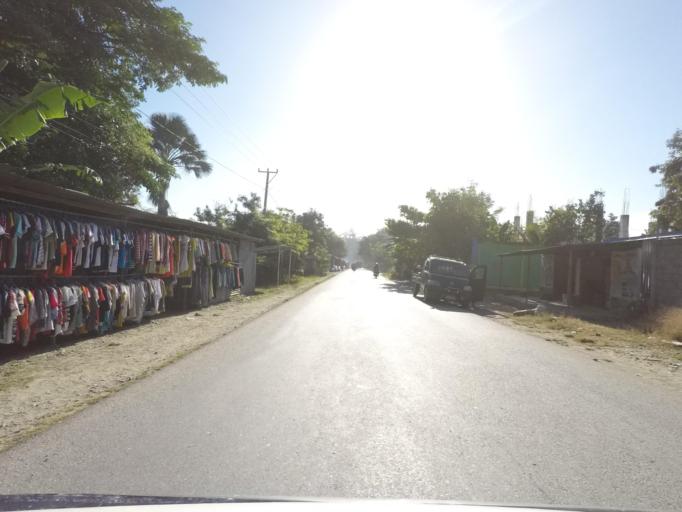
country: ID
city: Metinaro
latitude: -8.5511
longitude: 125.6621
